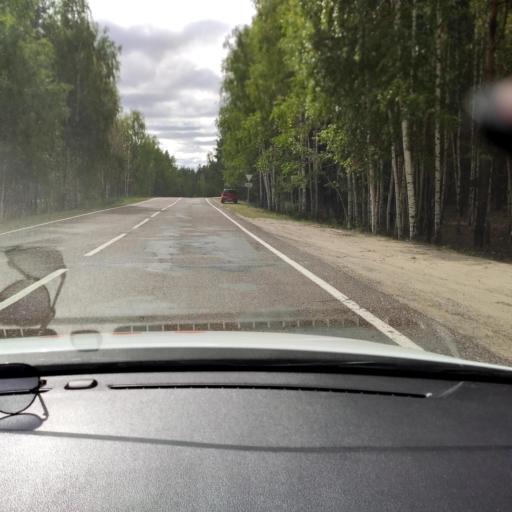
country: RU
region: Tatarstan
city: Stolbishchi
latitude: 55.6384
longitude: 49.1070
